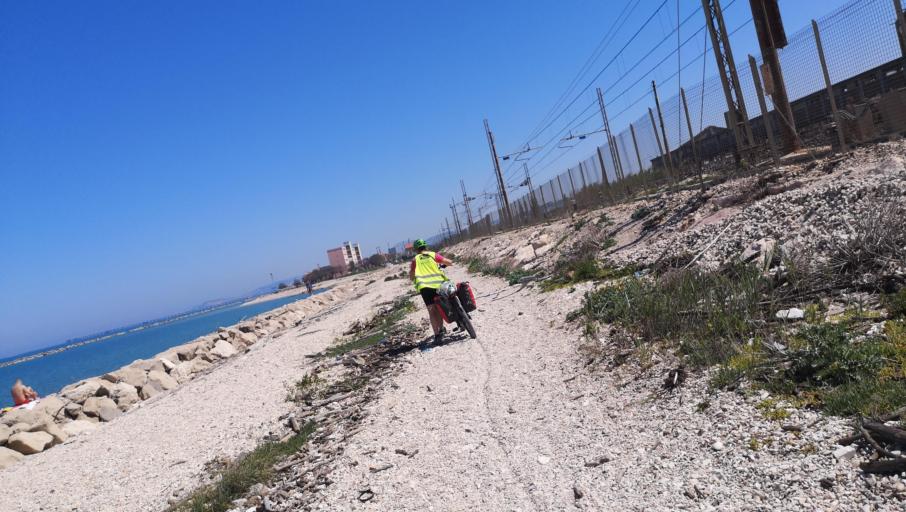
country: IT
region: The Marches
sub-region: Provincia di Ancona
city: Marina di Montemarciano
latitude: 43.6491
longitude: 13.3522
